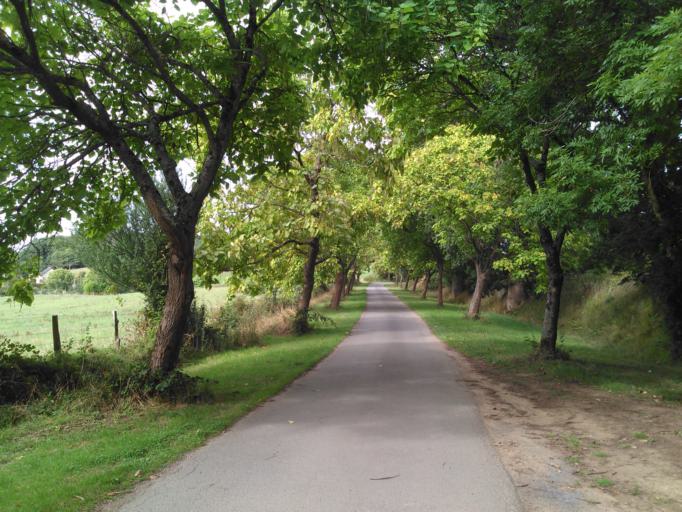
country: FR
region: Pays de la Loire
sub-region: Departement de la Mayenne
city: Laval
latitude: 48.0512
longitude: -0.7584
